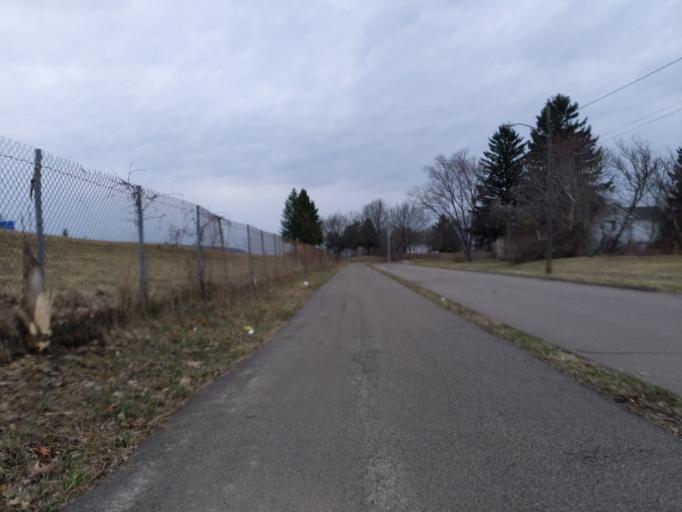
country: US
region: New York
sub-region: Chemung County
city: Elmira
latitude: 42.1094
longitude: -76.8127
